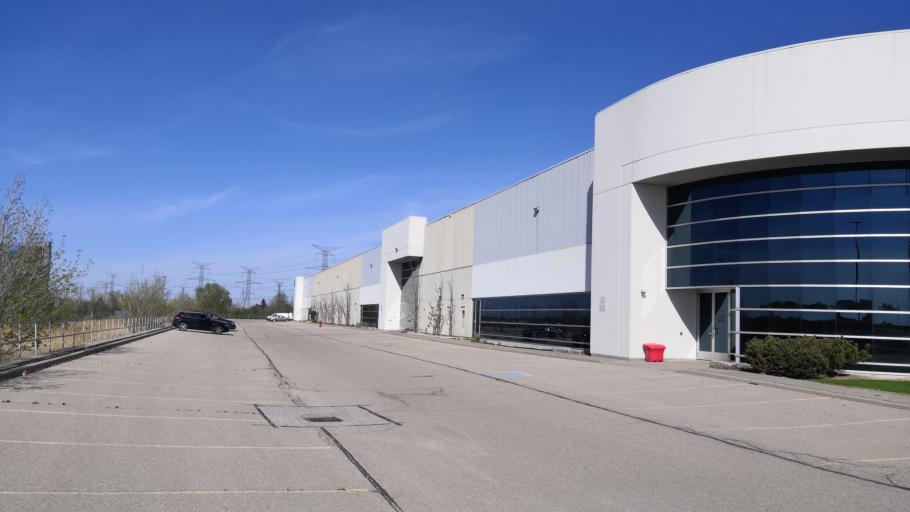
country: CA
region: Ontario
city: Concord
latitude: 43.7945
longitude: -79.4893
